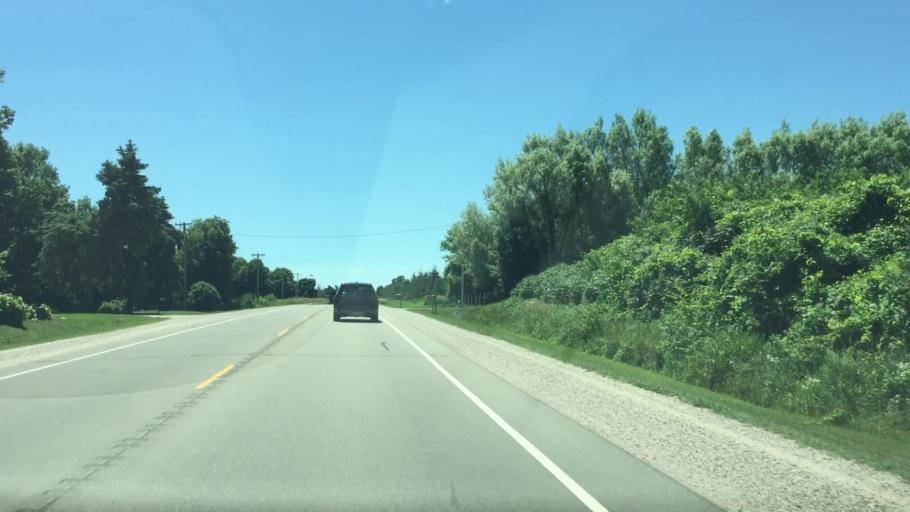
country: US
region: Wisconsin
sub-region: Calumet County
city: New Holstein
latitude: 43.9693
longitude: -88.1124
